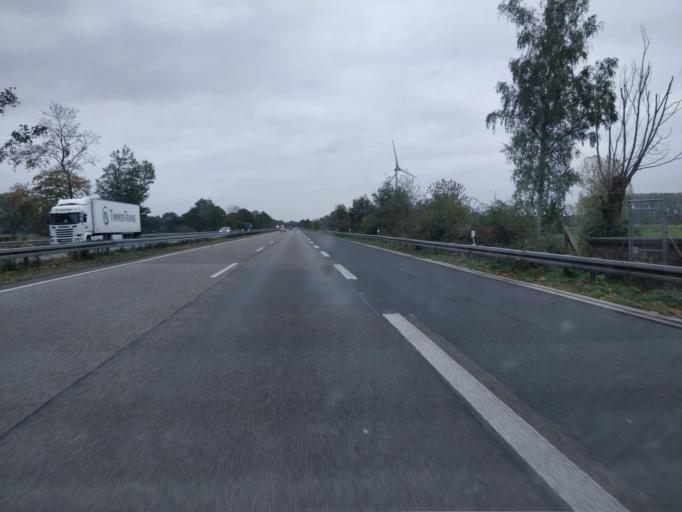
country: DE
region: North Rhine-Westphalia
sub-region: Regierungsbezirk Munster
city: Isselburg
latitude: 51.8090
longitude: 6.4658
